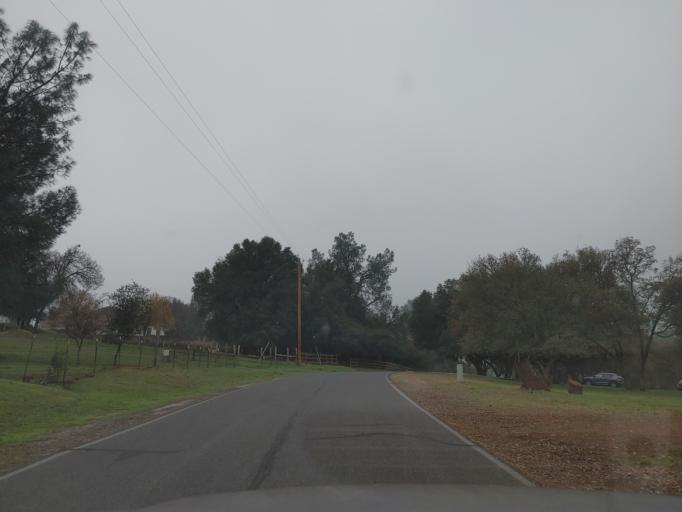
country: US
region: California
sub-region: Calaveras County
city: Copperopolis
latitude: 37.9416
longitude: -120.6117
